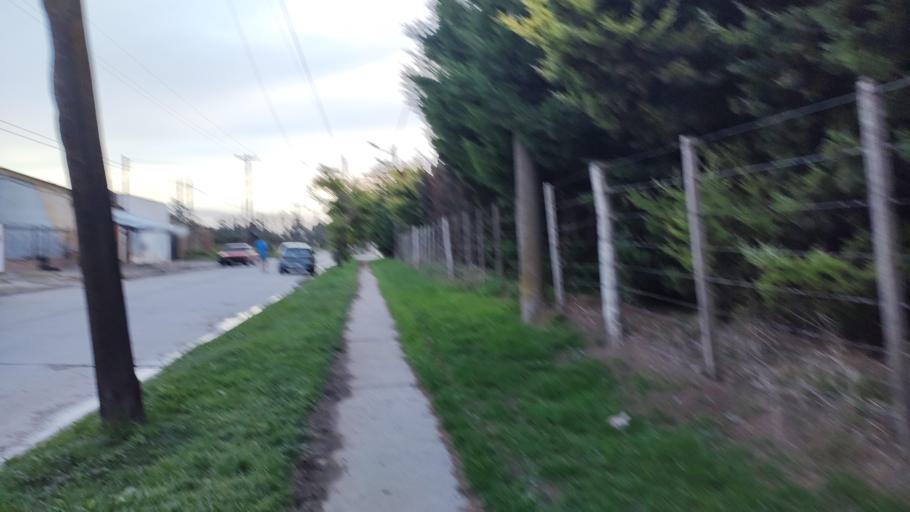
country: AR
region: Buenos Aires
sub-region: Partido de Loberia
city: Loberia
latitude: -38.1761
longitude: -58.7766
